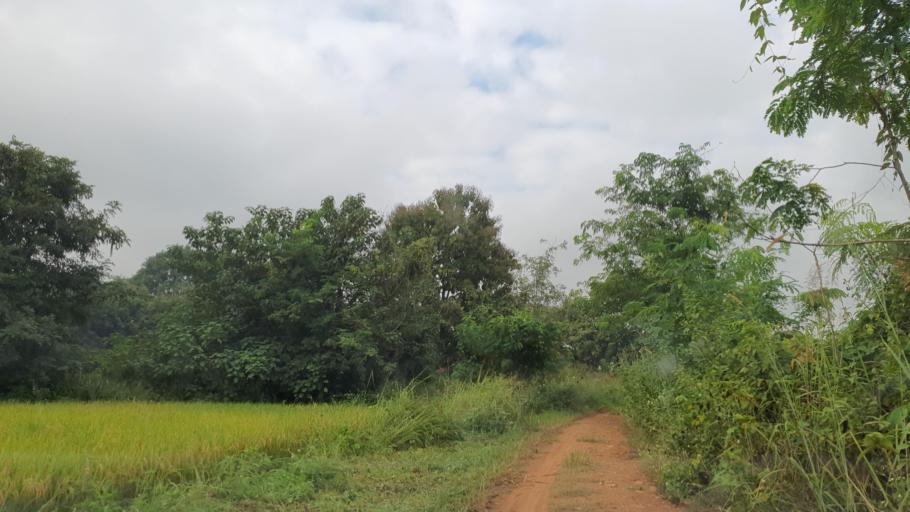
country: TH
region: Chiang Mai
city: San Kamphaeng
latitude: 18.7299
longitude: 99.1815
